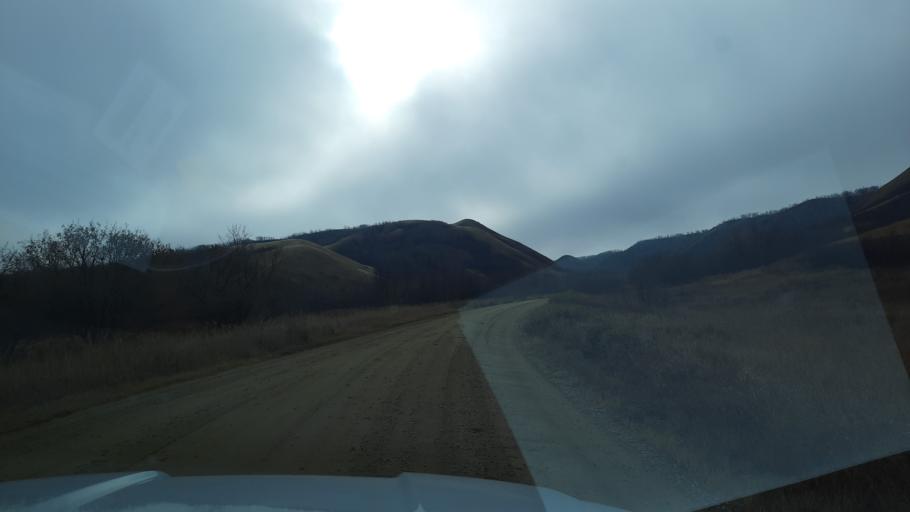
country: CA
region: Saskatchewan
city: White City
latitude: 50.7803
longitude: -104.1348
